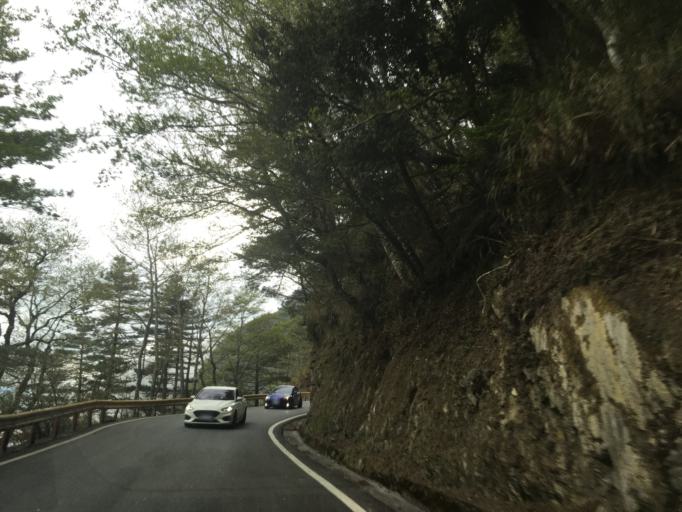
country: TW
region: Taiwan
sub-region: Hualien
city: Hualian
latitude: 24.1735
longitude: 121.3788
